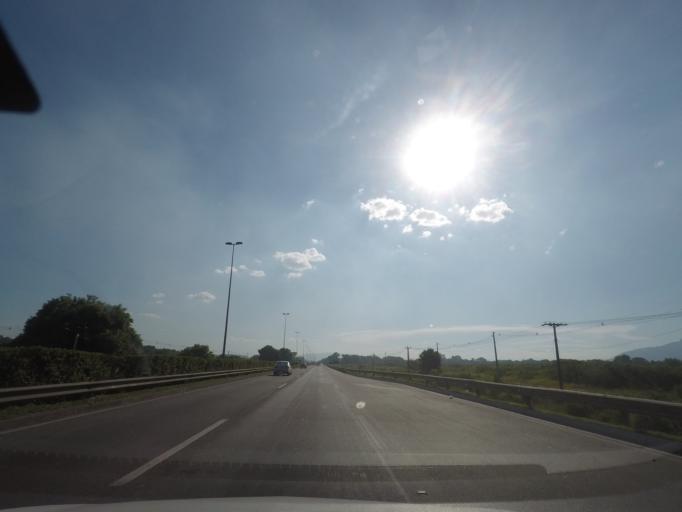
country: BR
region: Rio de Janeiro
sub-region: Duque De Caxias
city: Duque de Caxias
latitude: -22.6568
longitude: -43.2467
